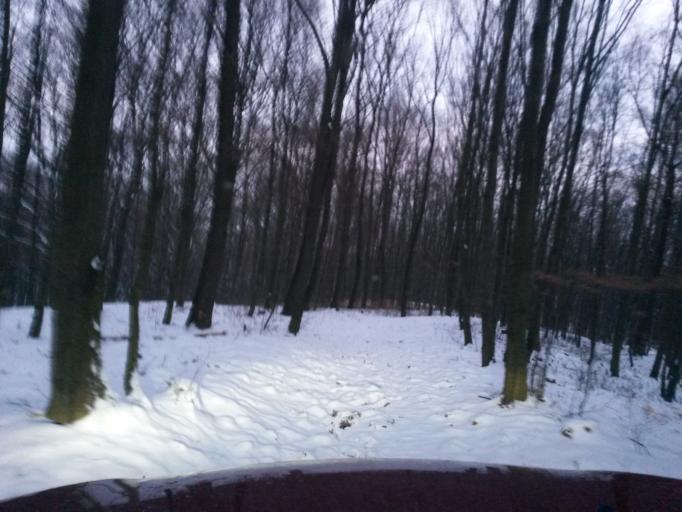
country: SK
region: Kosicky
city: Kosice
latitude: 48.7352
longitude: 21.3213
